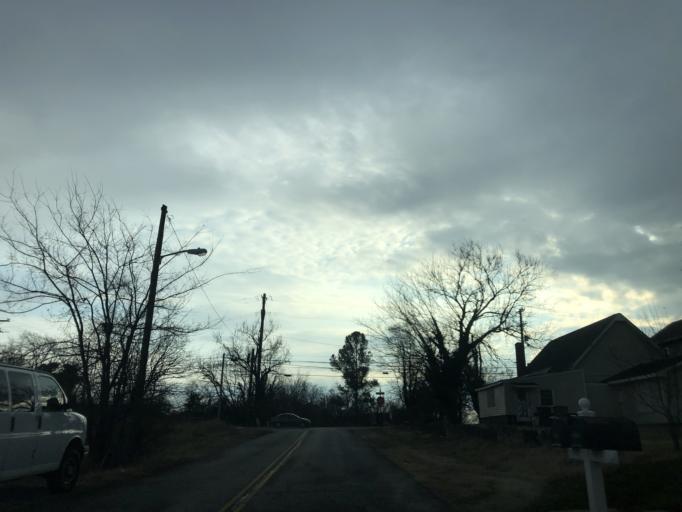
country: US
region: Tennessee
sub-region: Davidson County
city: Nashville
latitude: 36.2026
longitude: -86.7355
